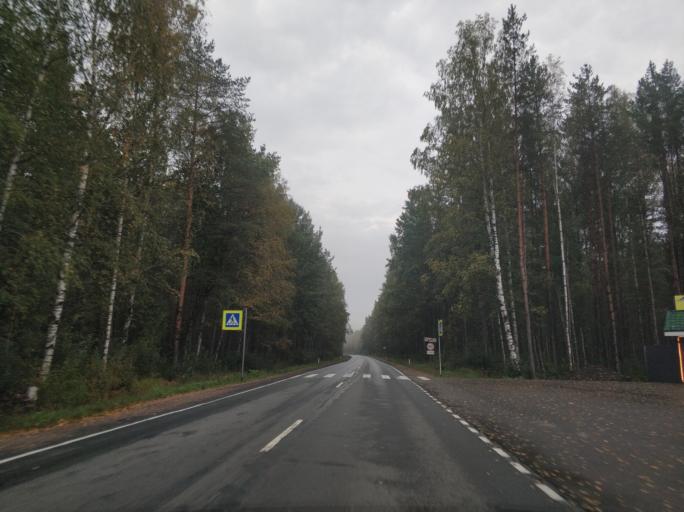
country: RU
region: Leningrad
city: Shcheglovo
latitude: 60.0920
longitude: 30.8554
